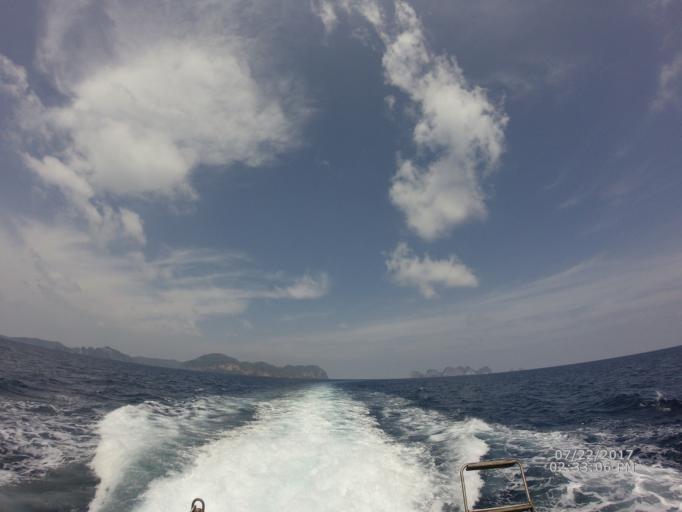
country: TH
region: Phangnga
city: Ban Phru Nai
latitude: 7.7413
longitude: 98.7106
